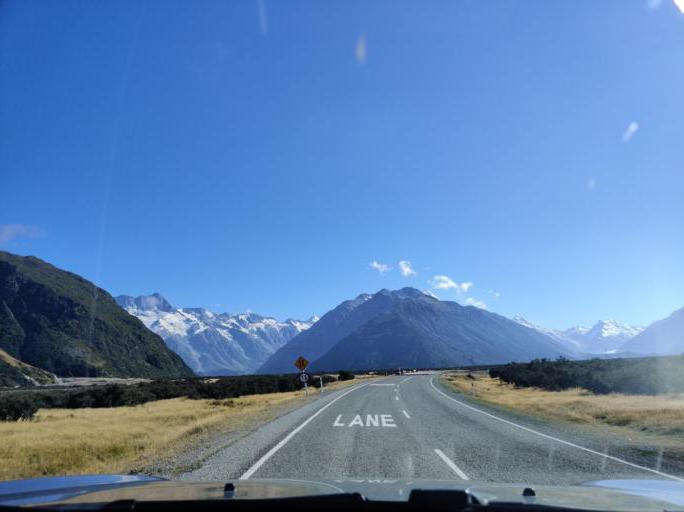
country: NZ
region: Canterbury
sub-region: Timaru District
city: Pleasant Point
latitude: -43.7707
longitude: 170.1229
